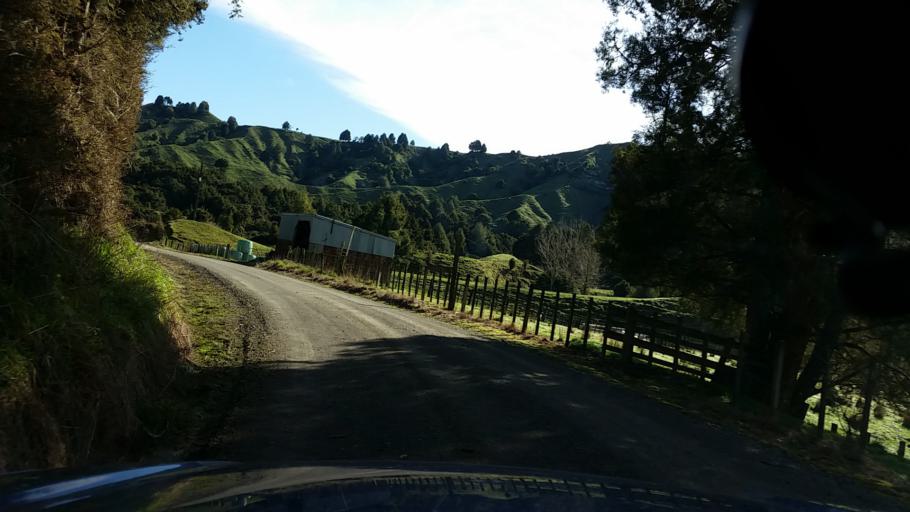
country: NZ
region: Taranaki
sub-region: New Plymouth District
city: Waitara
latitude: -39.0510
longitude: 174.7676
